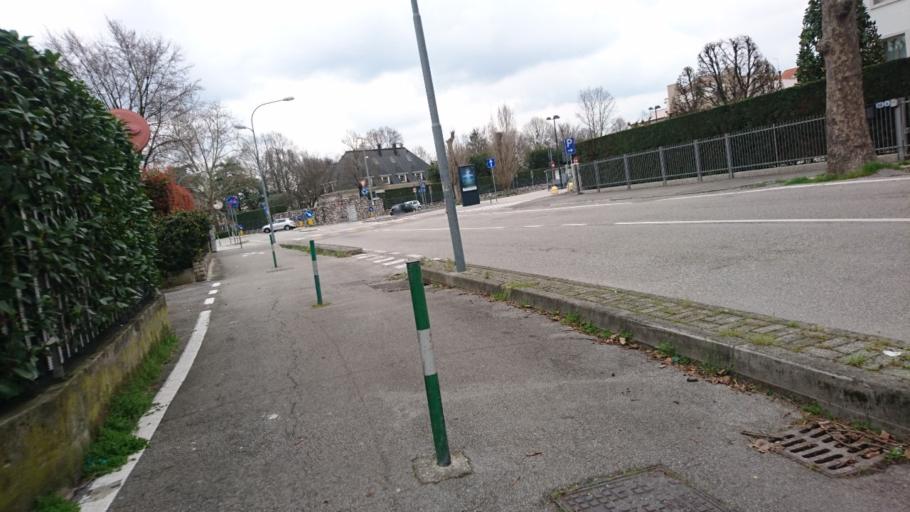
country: IT
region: Veneto
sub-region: Provincia di Padova
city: Vigodarzere
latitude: 45.4477
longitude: 11.8717
